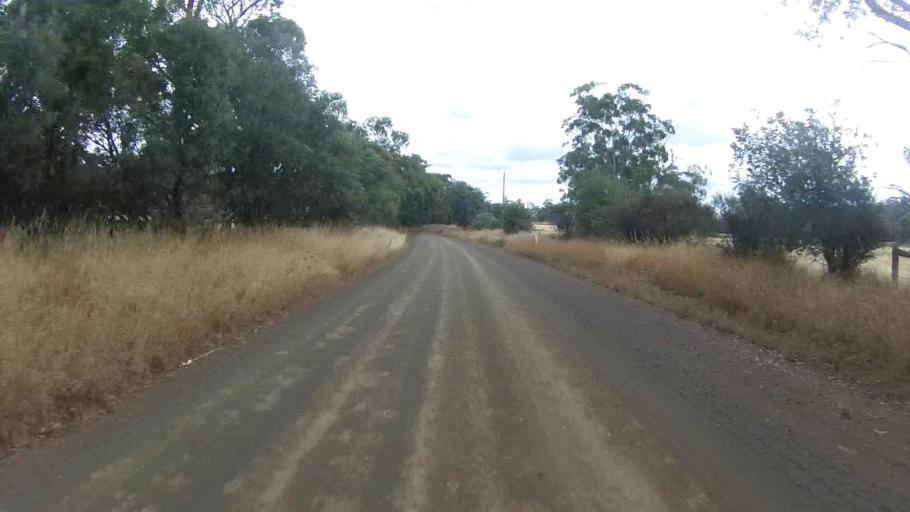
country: AU
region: Tasmania
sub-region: Break O'Day
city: St Helens
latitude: -41.8254
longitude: 147.9828
